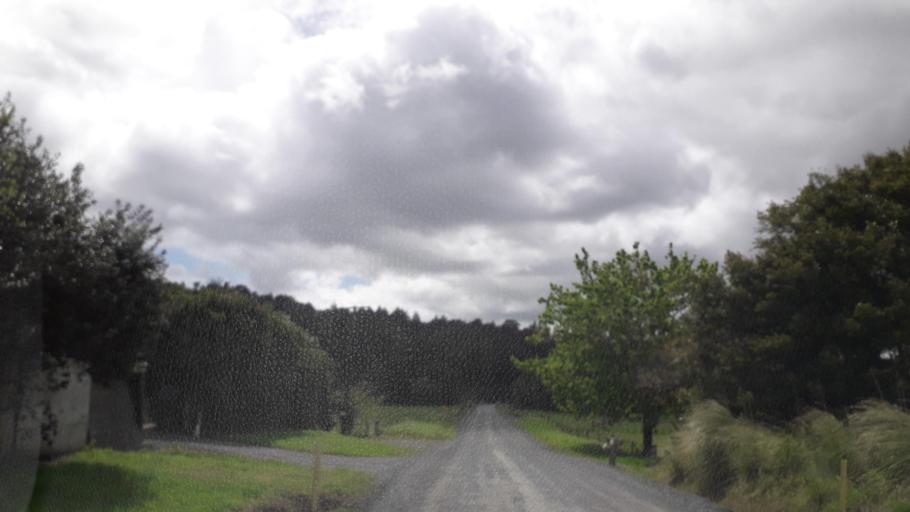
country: NZ
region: Northland
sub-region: Far North District
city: Kaitaia
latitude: -35.1721
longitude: 173.3317
